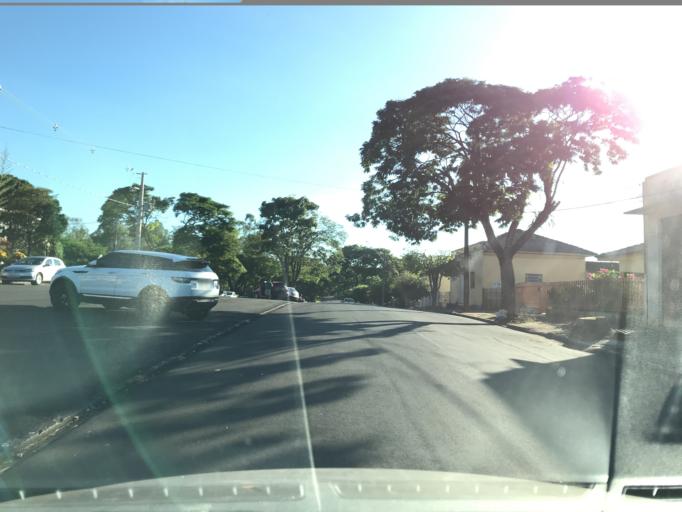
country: BR
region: Parana
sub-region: Ipora
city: Ipora
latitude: -24.0026
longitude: -53.7160
